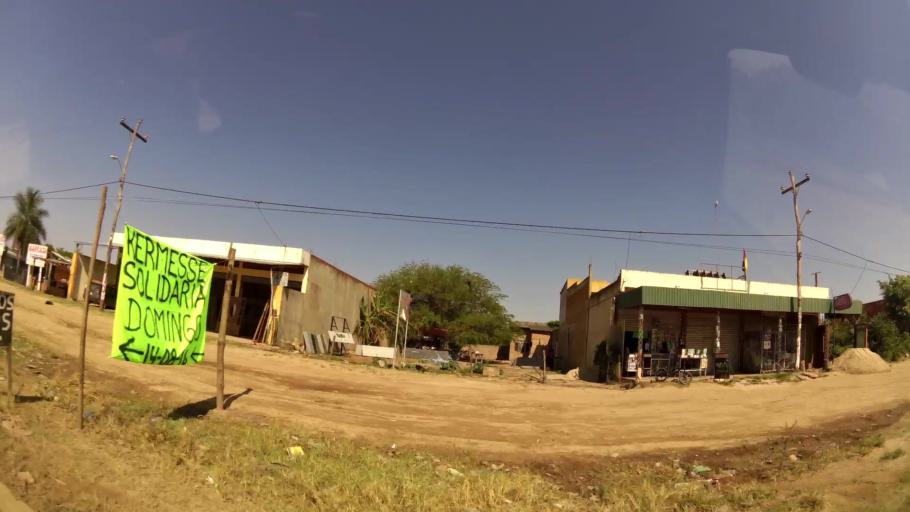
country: BO
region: Santa Cruz
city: Cotoca
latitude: -17.7312
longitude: -63.0947
